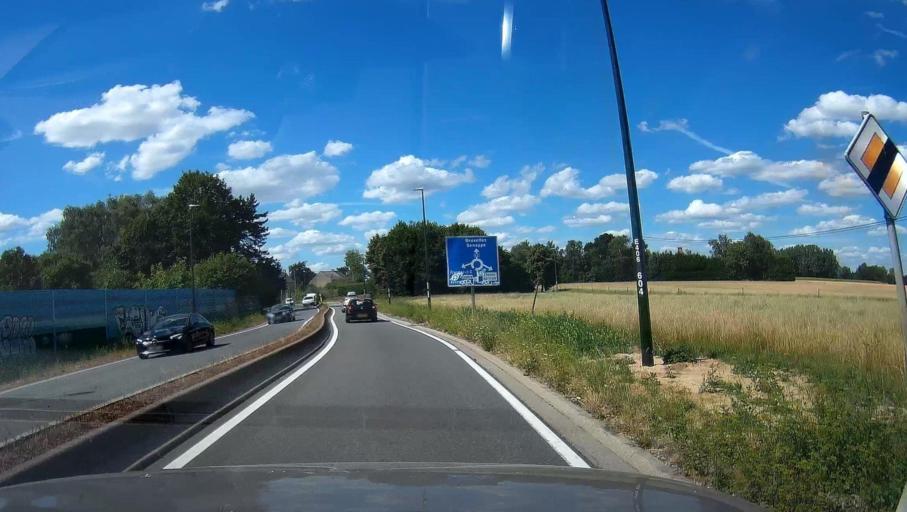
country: BE
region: Wallonia
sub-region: Province du Hainaut
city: Brunehault
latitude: 50.5494
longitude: 4.4539
